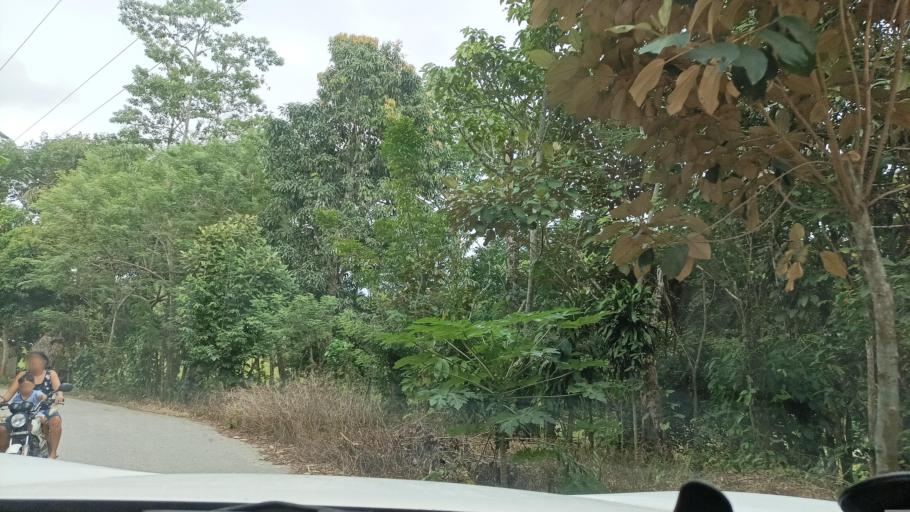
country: MX
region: Veracruz
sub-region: Moloacan
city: Cuichapa
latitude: 17.8510
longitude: -94.3533
